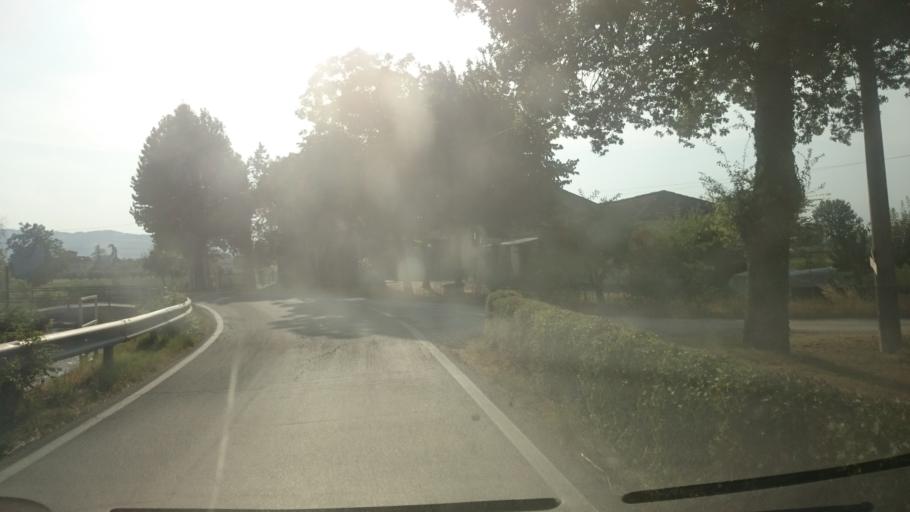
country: IT
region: Emilia-Romagna
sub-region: Provincia di Reggio Emilia
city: Arceto
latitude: 44.6002
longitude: 10.7196
